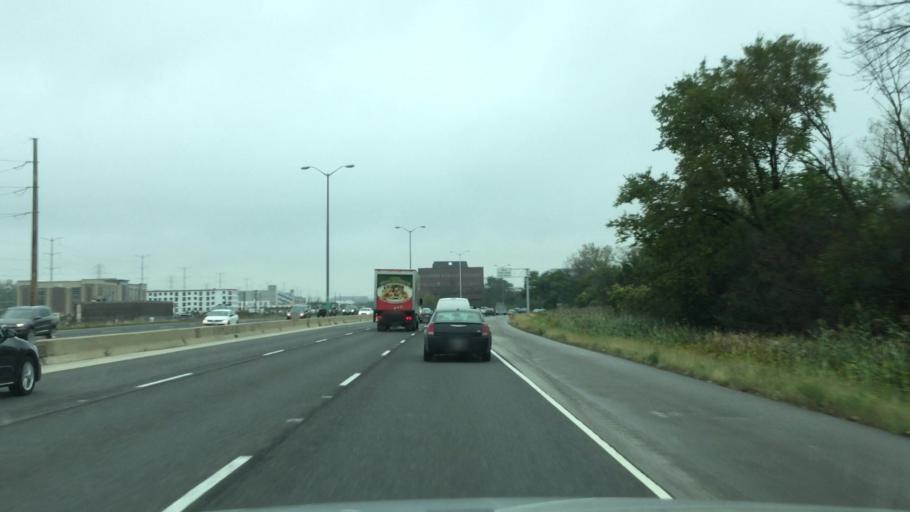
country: US
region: Illinois
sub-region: Cook County
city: Northfield
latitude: 42.1264
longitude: -87.7838
